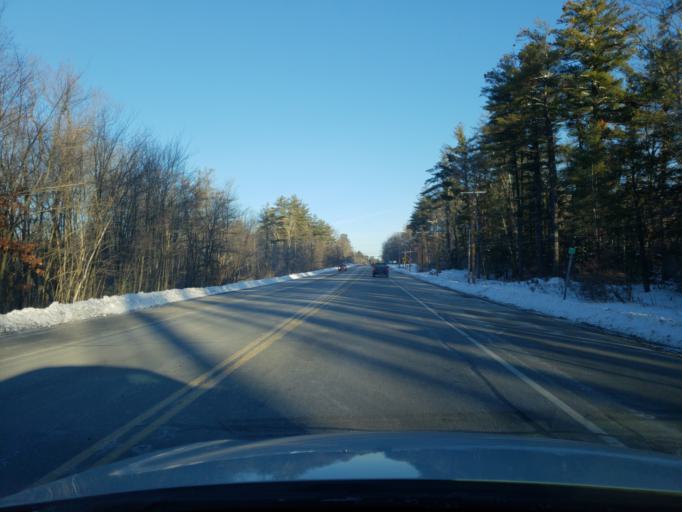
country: US
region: New Hampshire
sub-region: Hillsborough County
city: Pinardville
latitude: 42.9873
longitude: -71.5225
